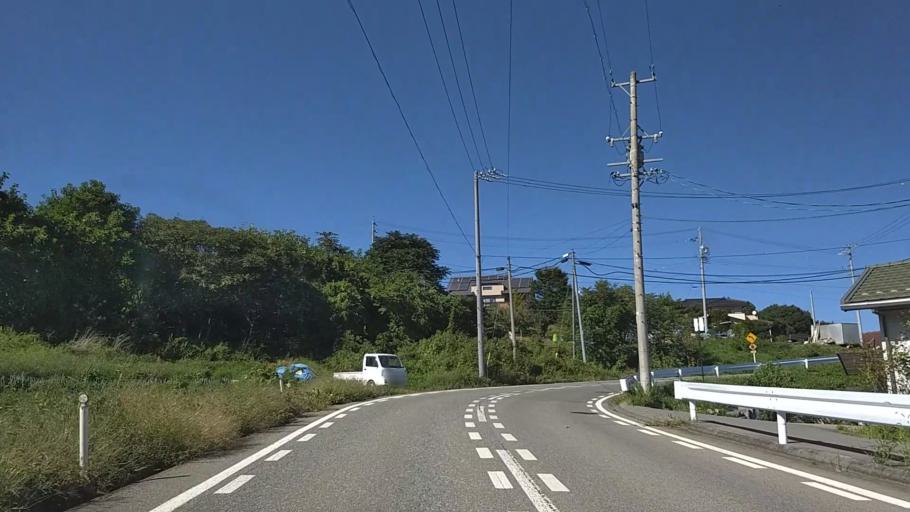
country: JP
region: Nagano
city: Nagano-shi
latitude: 36.5841
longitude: 138.1114
